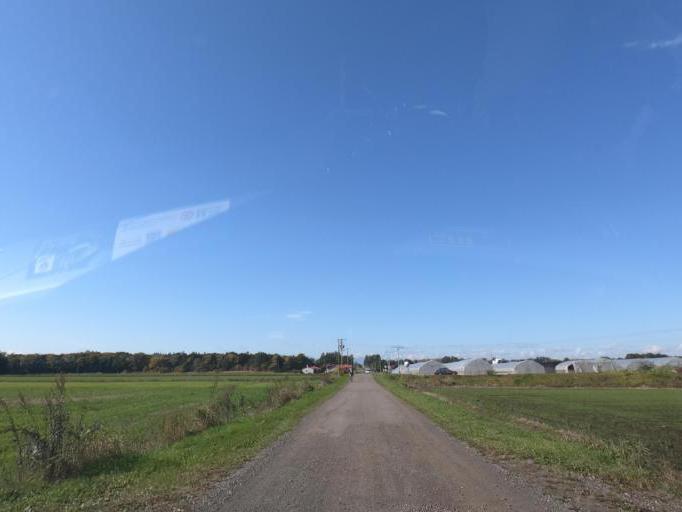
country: JP
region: Hokkaido
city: Obihiro
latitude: 42.9502
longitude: 143.2471
